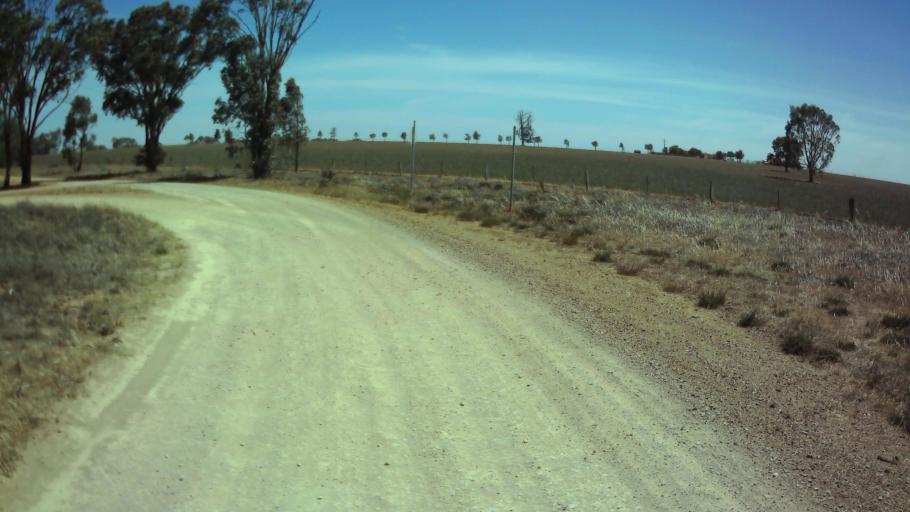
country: AU
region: New South Wales
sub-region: Weddin
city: Grenfell
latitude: -33.9231
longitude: 148.1777
